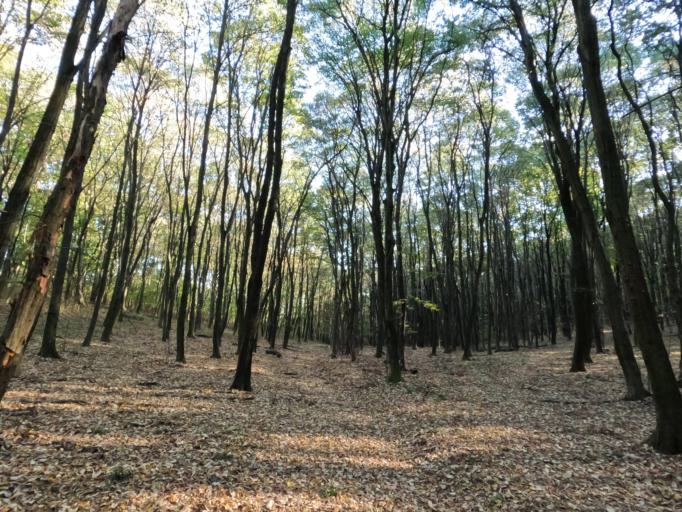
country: HU
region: Tolna
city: Szentgalpuszta
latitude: 46.3116
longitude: 18.6522
